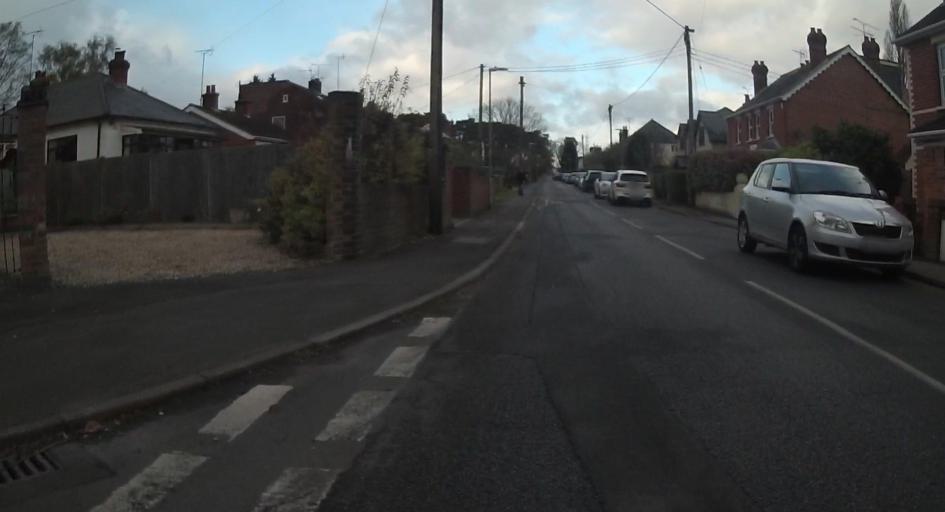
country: GB
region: England
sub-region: Bracknell Forest
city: Sandhurst
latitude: 51.3538
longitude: -0.7816
